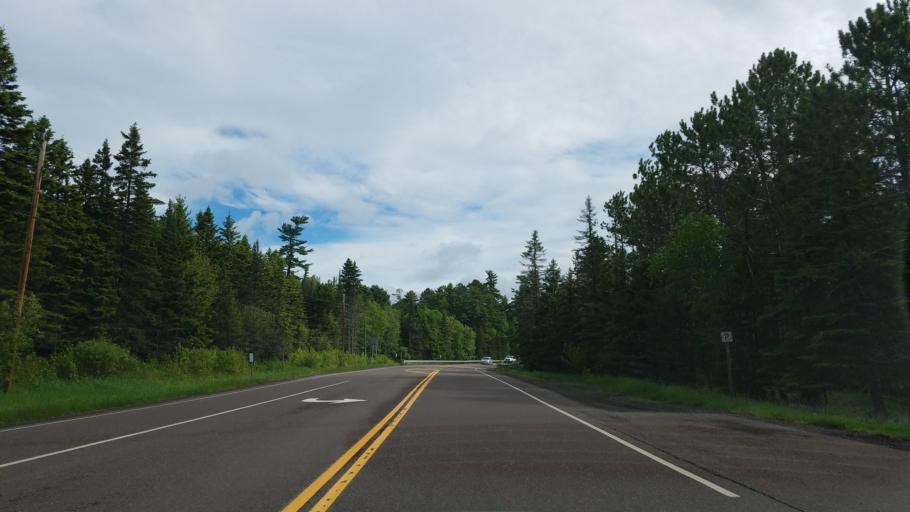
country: US
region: Minnesota
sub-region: Lake County
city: Two Harbors
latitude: 47.0915
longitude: -91.5770
